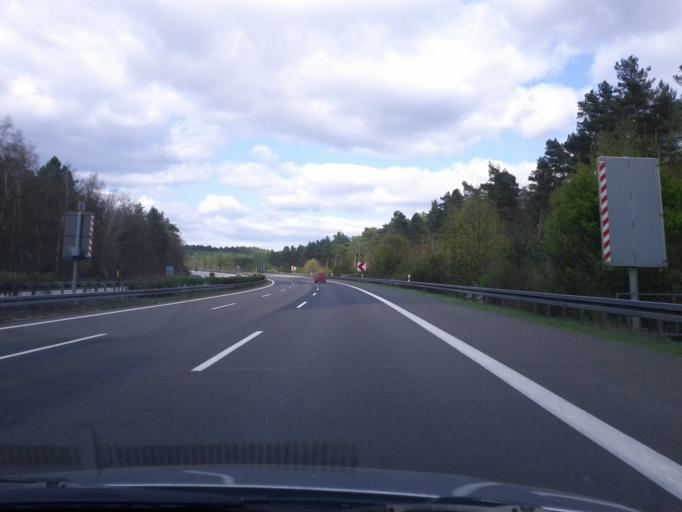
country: DE
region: Brandenburg
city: Grunheide
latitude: 52.4403
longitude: 13.7999
